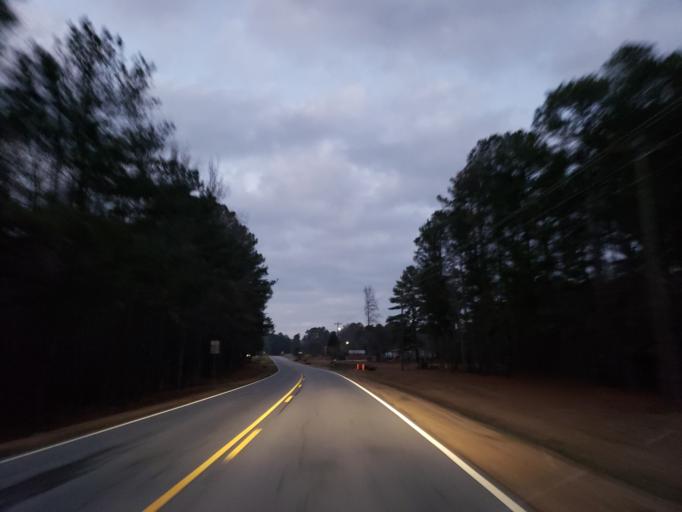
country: US
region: Georgia
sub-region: Carroll County
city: Temple
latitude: 33.7791
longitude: -85.0622
